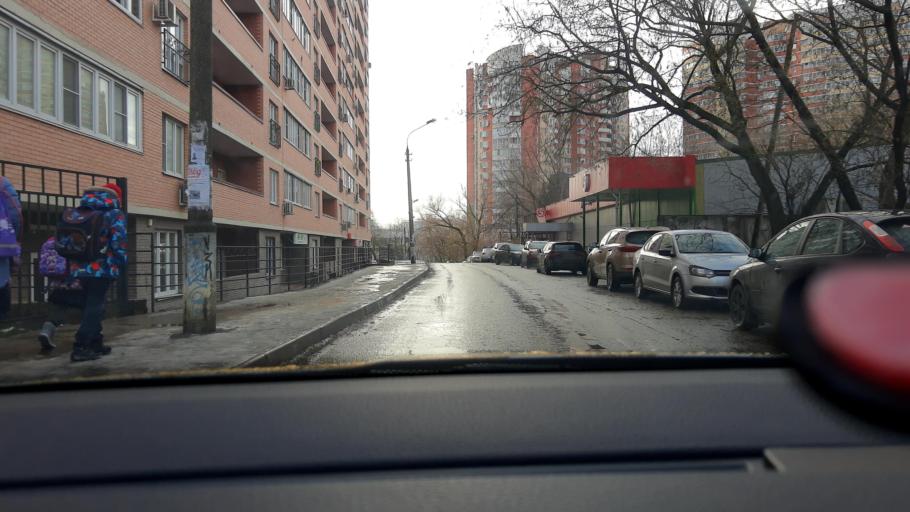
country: RU
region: Moskovskaya
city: Pushkino
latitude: 55.9982
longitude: 37.8659
